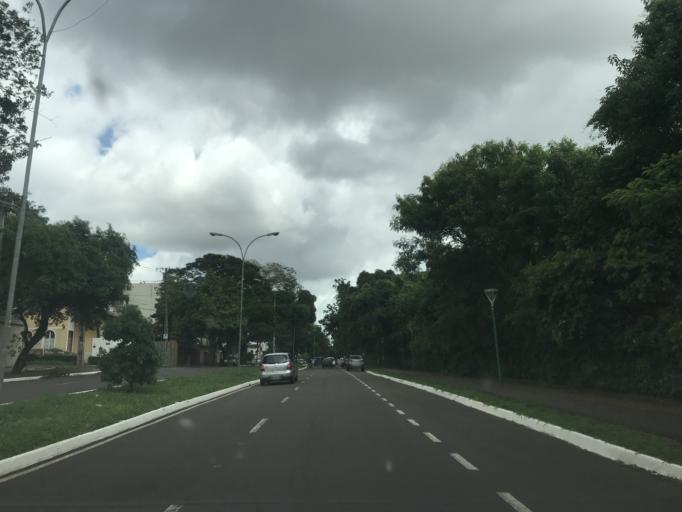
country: BR
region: Parana
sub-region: Maringa
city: Maringa
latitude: -23.4333
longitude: -51.9453
